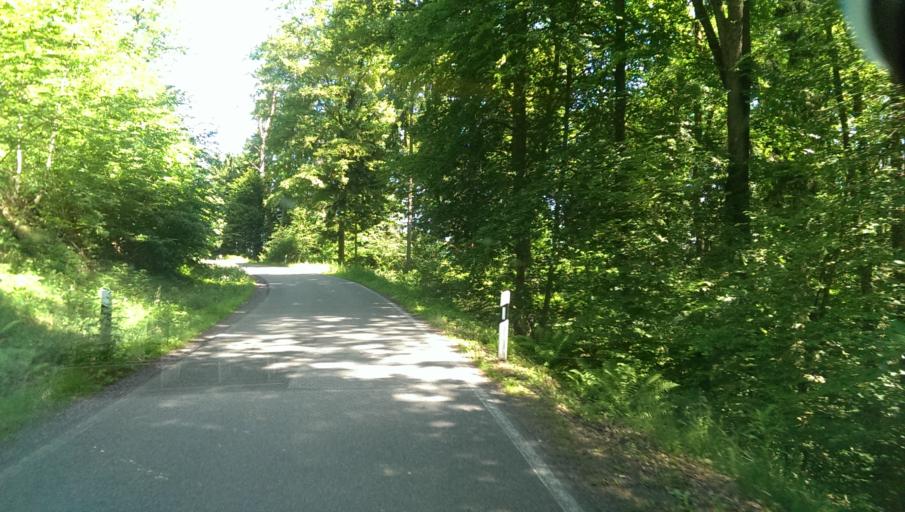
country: DE
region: Rheinland-Pfalz
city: Nothweiler
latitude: 49.0777
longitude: 7.7966
